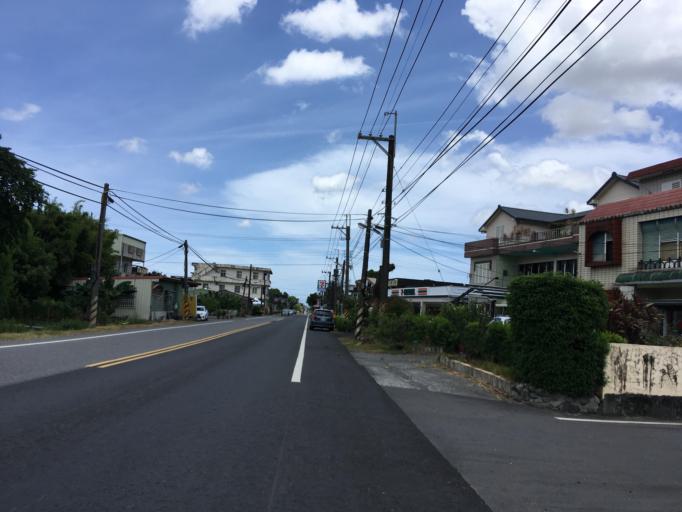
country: TW
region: Taiwan
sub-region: Yilan
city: Yilan
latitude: 24.7004
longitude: 121.7405
